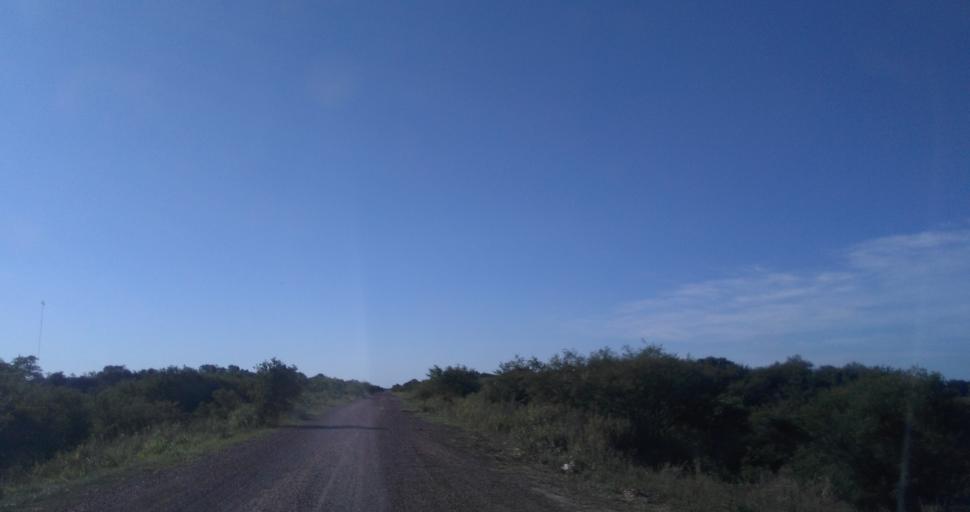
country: AR
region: Chaco
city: Barranqueras
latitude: -27.4220
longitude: -58.9331
